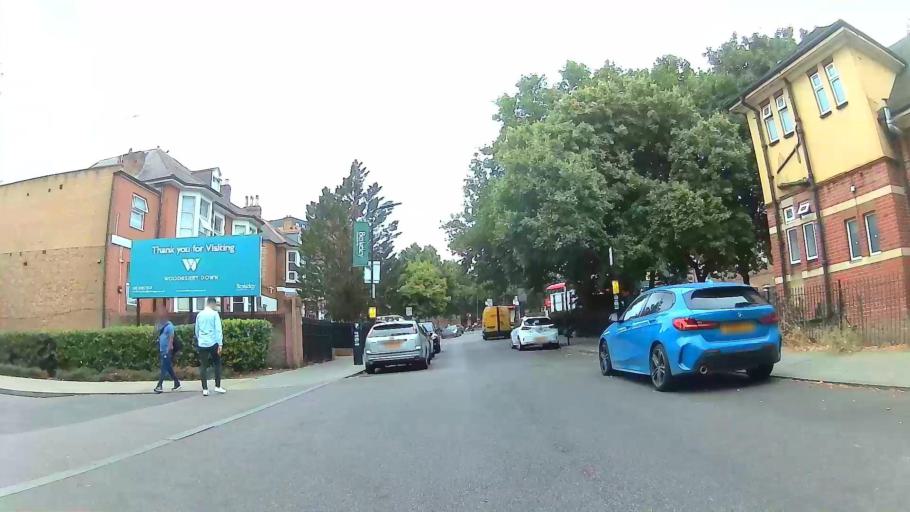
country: GB
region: England
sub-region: Greater London
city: Harringay
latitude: 51.5709
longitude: -0.0944
